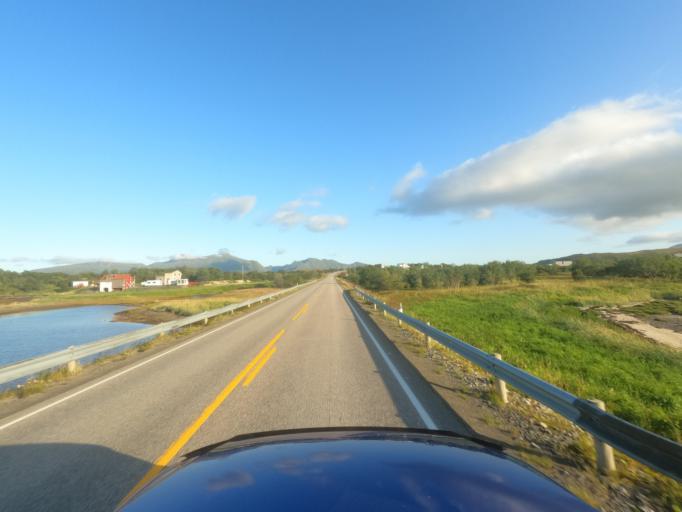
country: NO
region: Nordland
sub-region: Vestvagoy
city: Gravdal
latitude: 68.1532
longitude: 13.5367
